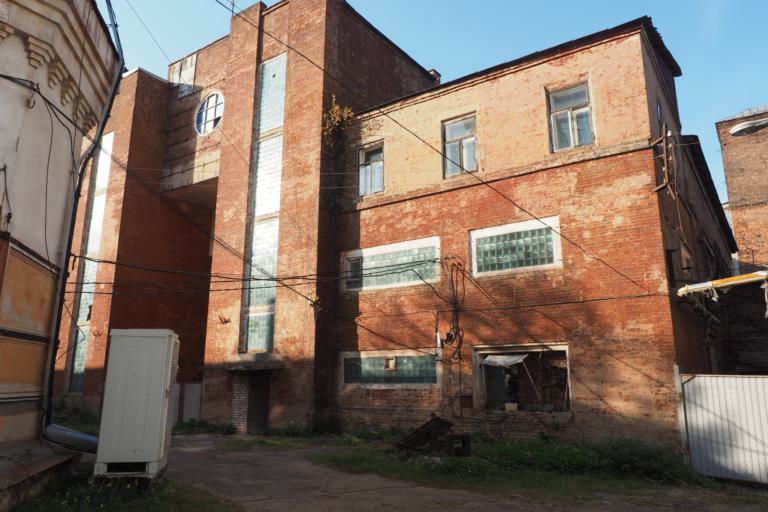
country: RU
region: Moskovskaya
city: Kurovskoye
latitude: 55.5798
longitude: 38.9181
